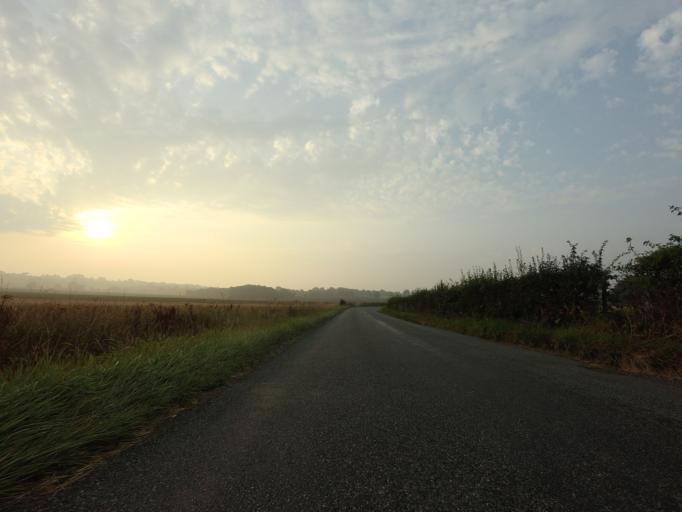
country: GB
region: England
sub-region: Kent
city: Lenham
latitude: 51.1726
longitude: 0.7323
